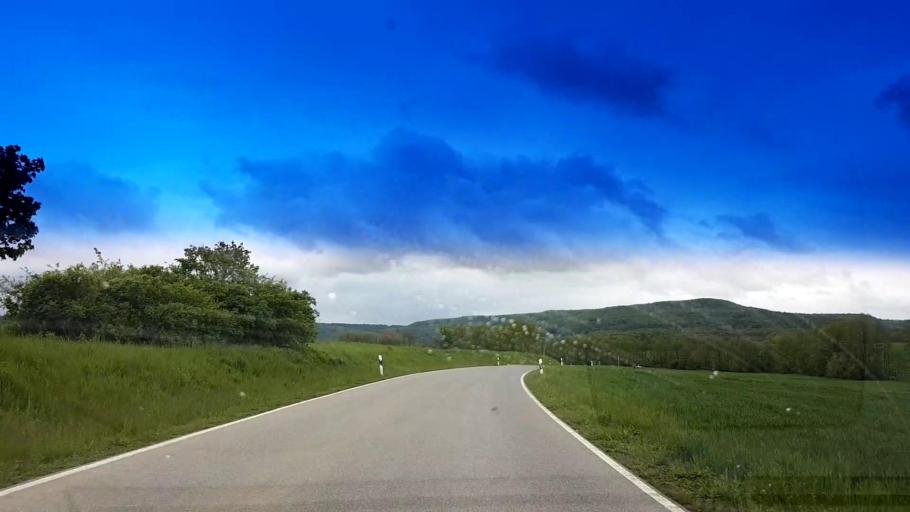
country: DE
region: Bavaria
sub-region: Upper Franconia
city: Schesslitz
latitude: 49.9582
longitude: 11.0091
